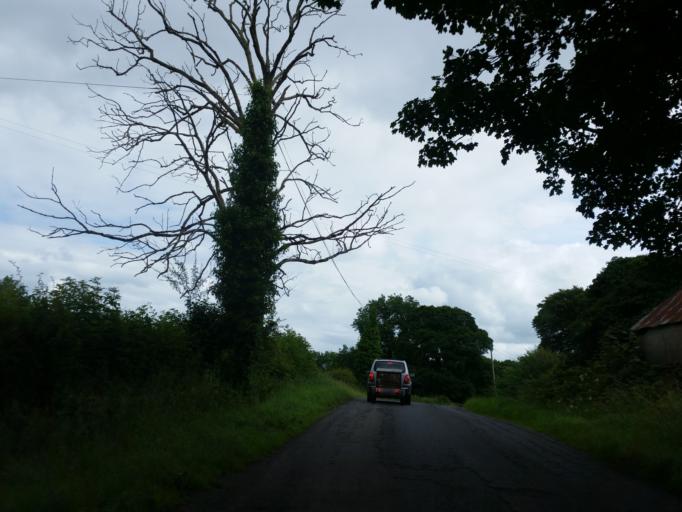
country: IE
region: Ulster
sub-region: County Monaghan
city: Clones
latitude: 54.2070
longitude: -7.2441
